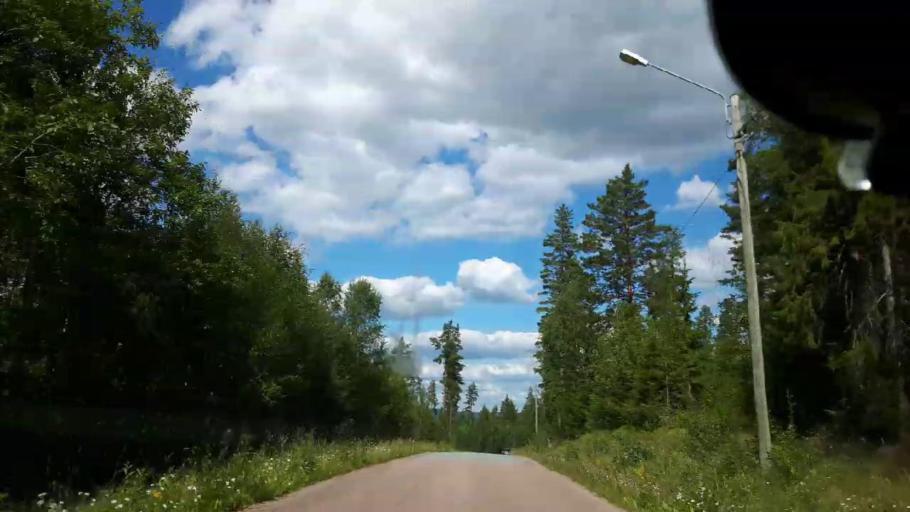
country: SE
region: Jaemtland
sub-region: Ragunda Kommun
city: Hammarstrand
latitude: 62.9320
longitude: 16.6935
